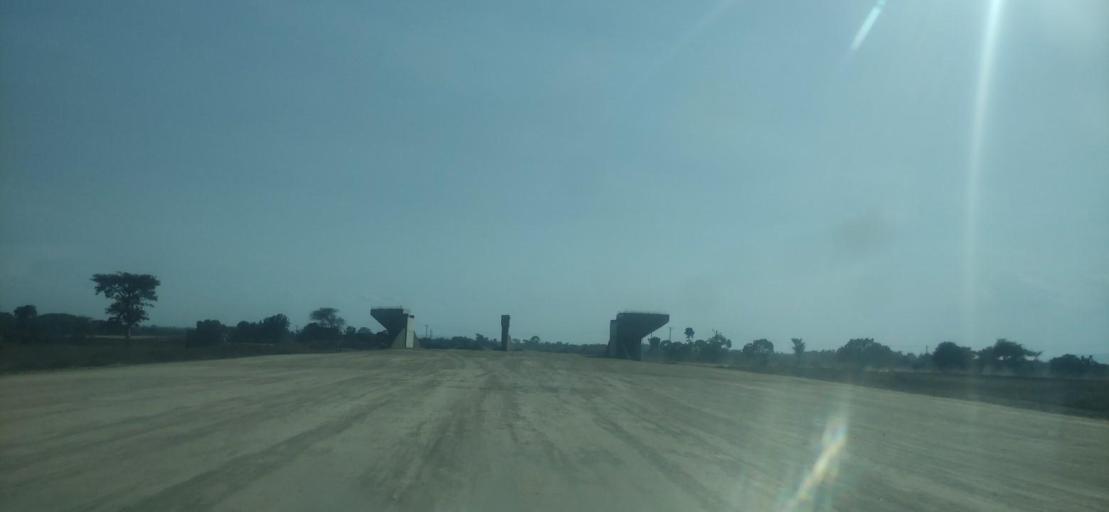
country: ET
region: Oromiya
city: Shashemene
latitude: 7.2574
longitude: 38.5945
